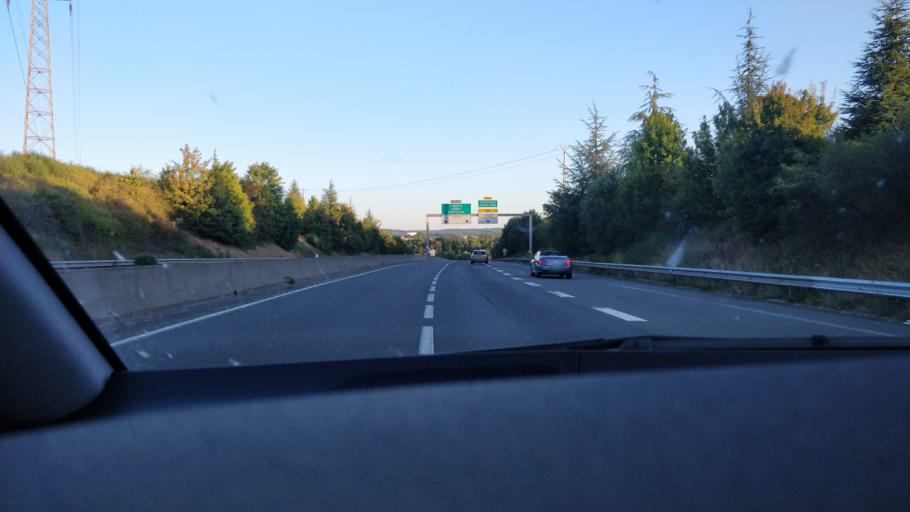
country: FR
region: Poitou-Charentes
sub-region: Departement de la Charente
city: Gond-Pontouvre
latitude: 45.6945
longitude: 0.1890
